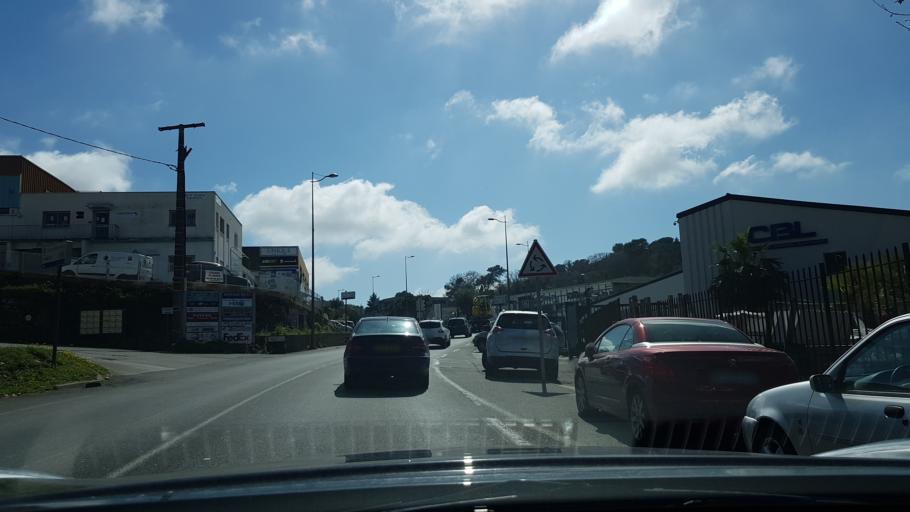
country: FR
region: Provence-Alpes-Cote d'Azur
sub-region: Departement des Alpes-Maritimes
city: Vallauris
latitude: 43.5941
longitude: 7.0574
